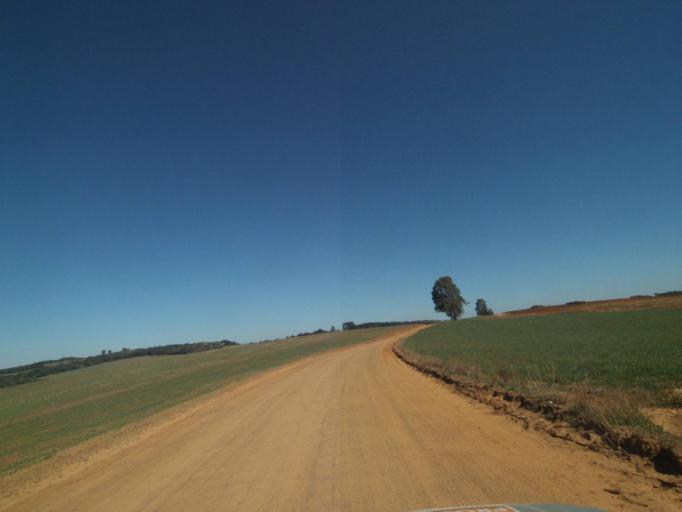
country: BR
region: Parana
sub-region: Tibagi
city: Tibagi
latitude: -24.5612
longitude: -50.6227
